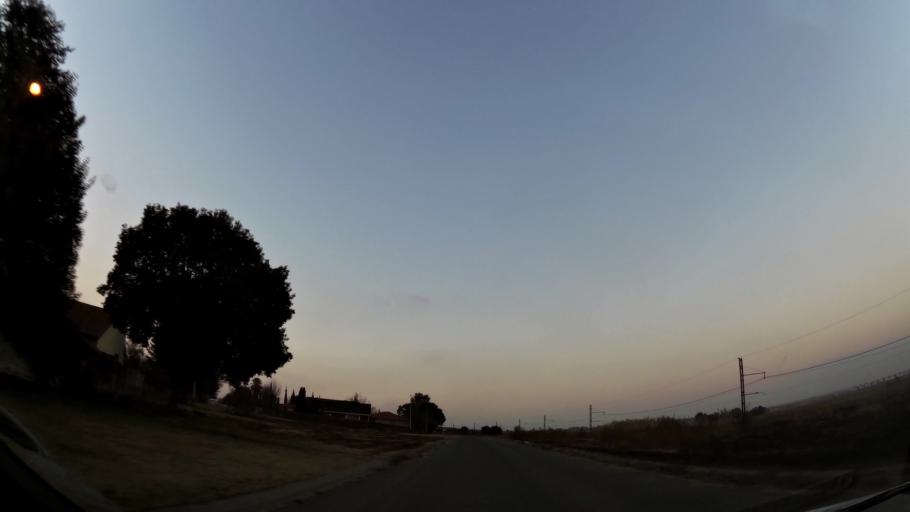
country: ZA
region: Gauteng
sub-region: Ekurhuleni Metropolitan Municipality
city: Nigel
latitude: -26.3566
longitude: 28.4398
